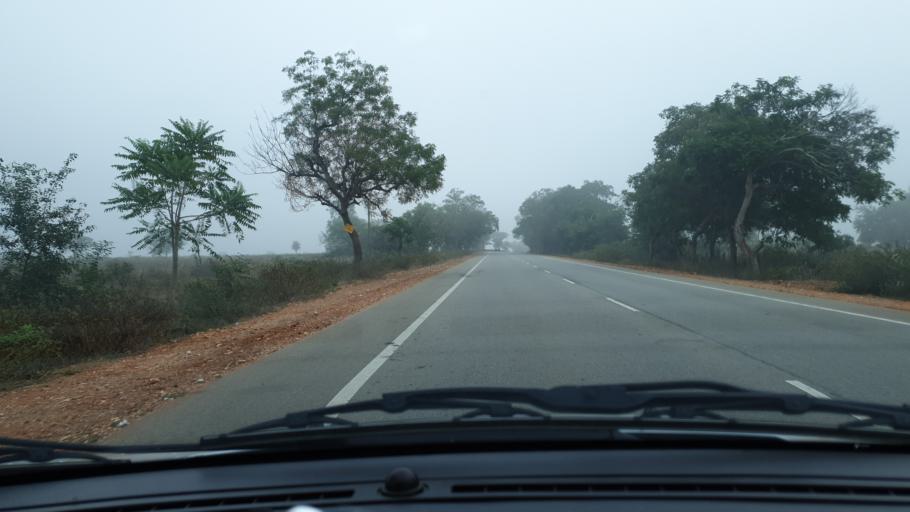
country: IN
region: Telangana
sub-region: Nalgonda
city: Devarkonda
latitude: 16.6320
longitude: 78.6142
